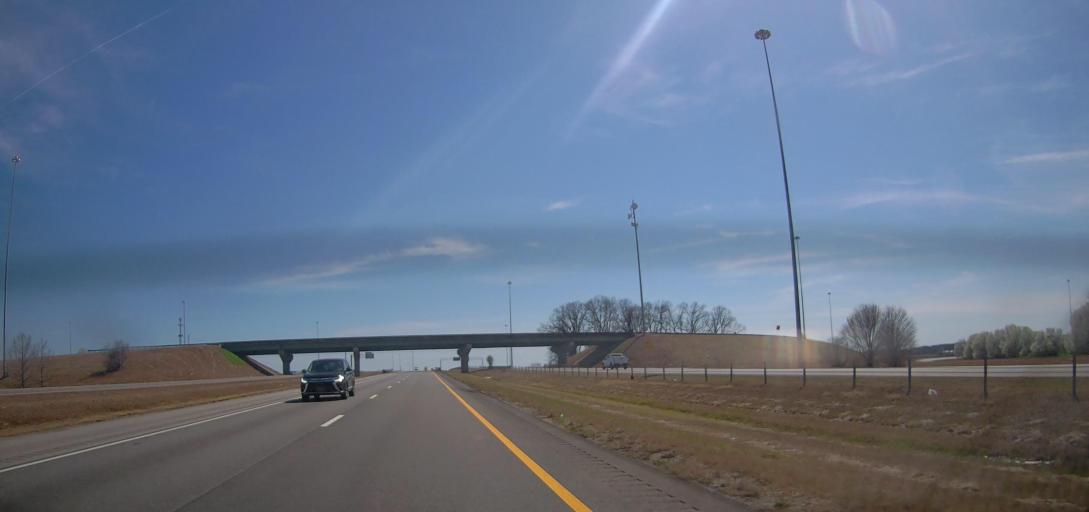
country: US
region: Alabama
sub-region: Morgan County
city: Decatur
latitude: 34.6312
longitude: -86.9019
